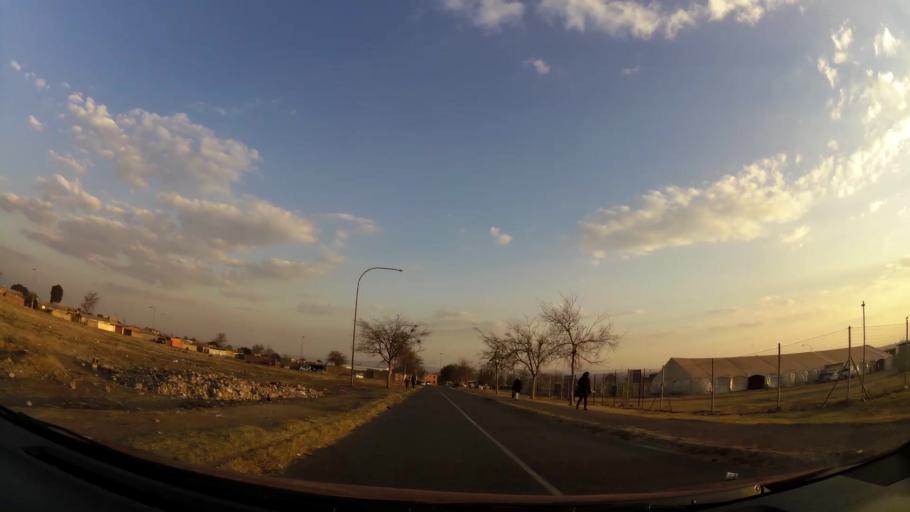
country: ZA
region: Gauteng
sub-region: City of Johannesburg Metropolitan Municipality
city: Soweto
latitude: -26.2304
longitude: 27.8965
